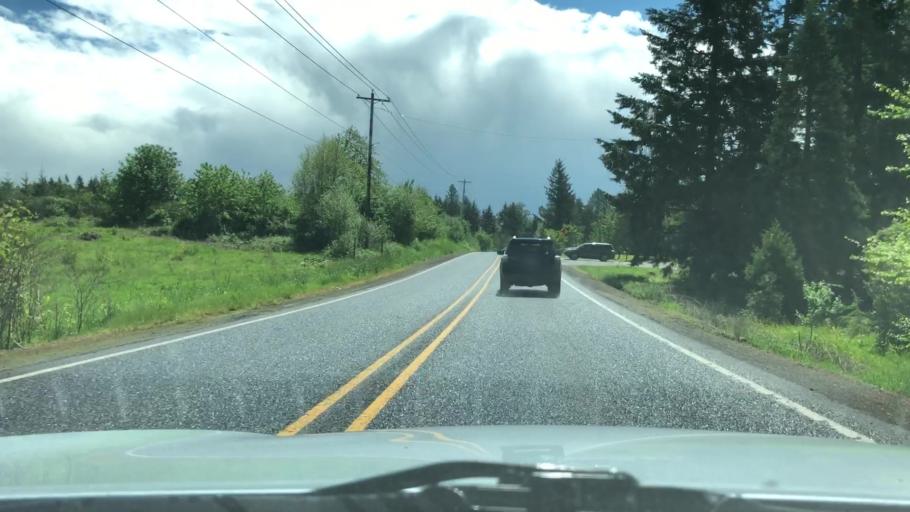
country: US
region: Oregon
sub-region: Clackamas County
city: Beavercreek
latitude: 45.3041
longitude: -122.5434
